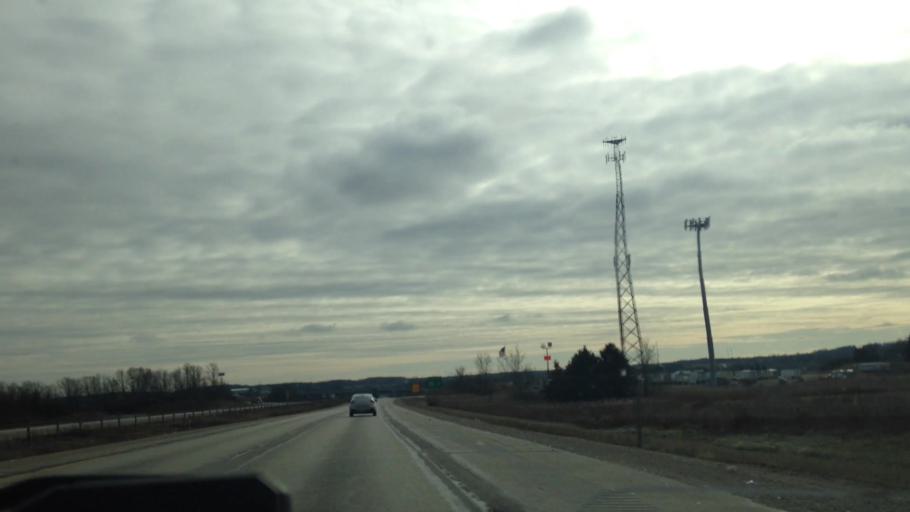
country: US
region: Wisconsin
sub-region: Washington County
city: Richfield
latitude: 43.2875
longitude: -88.2001
